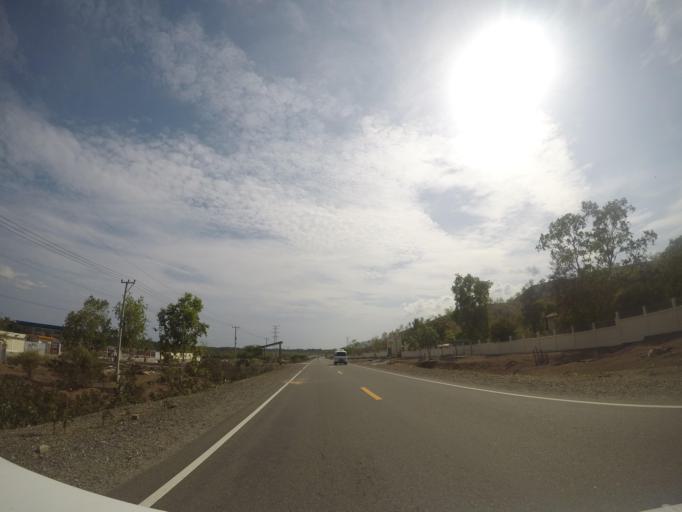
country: ID
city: Metinaro
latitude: -8.5136
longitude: 125.7824
